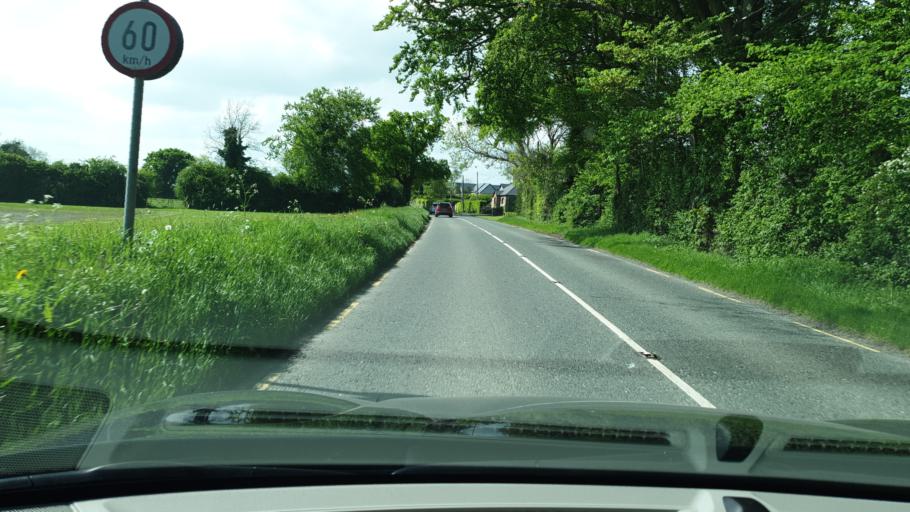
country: IE
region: Leinster
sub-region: An Mhi
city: Ratoath
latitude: 53.5113
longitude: -6.4773
